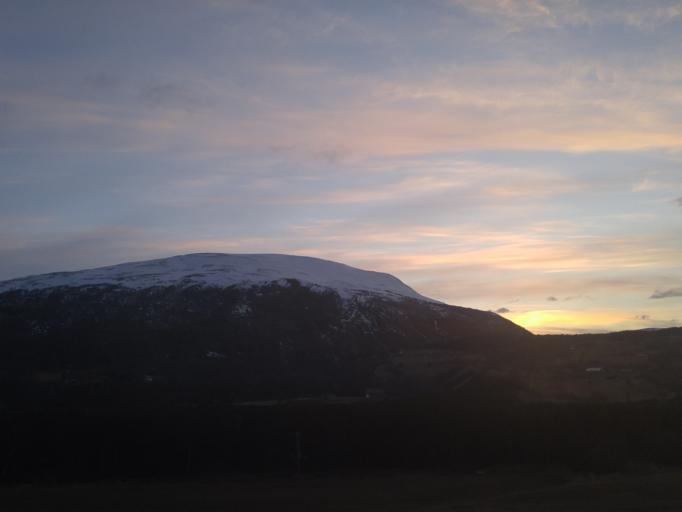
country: NO
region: Sor-Trondelag
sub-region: Oppdal
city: Oppdal
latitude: 62.5478
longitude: 9.6387
